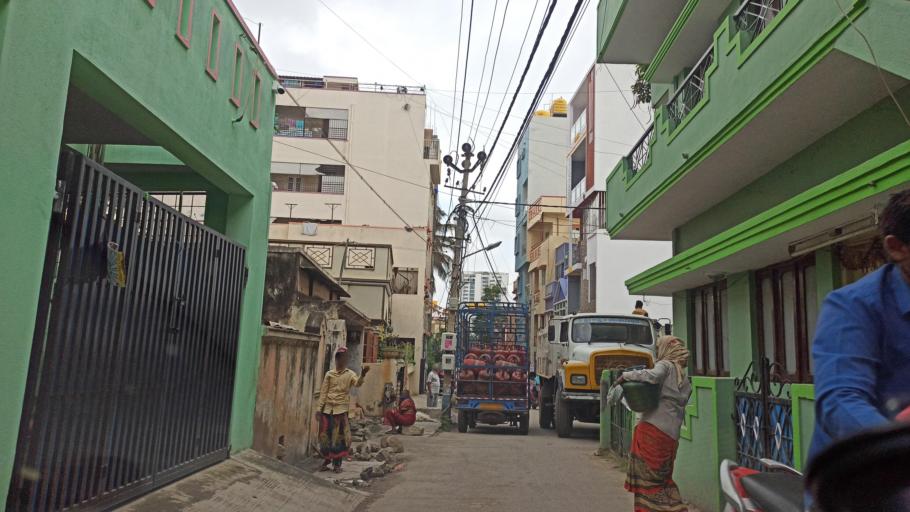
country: IN
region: Karnataka
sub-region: Bangalore Urban
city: Bangalore
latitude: 12.9935
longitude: 77.6742
